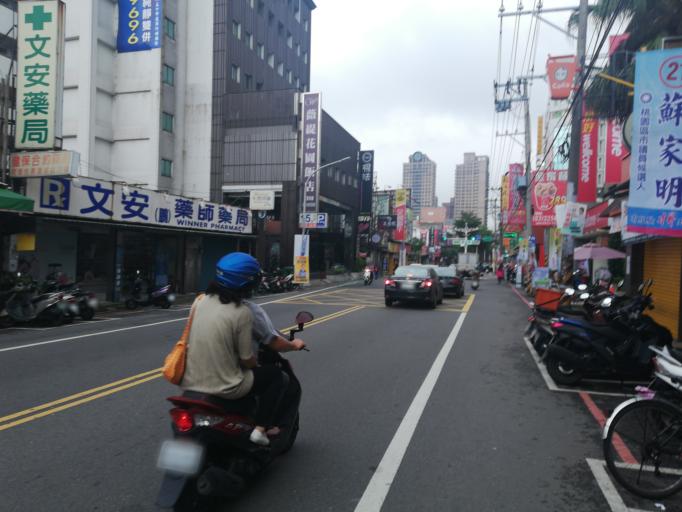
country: TW
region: Taiwan
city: Taoyuan City
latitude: 25.0067
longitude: 121.3035
